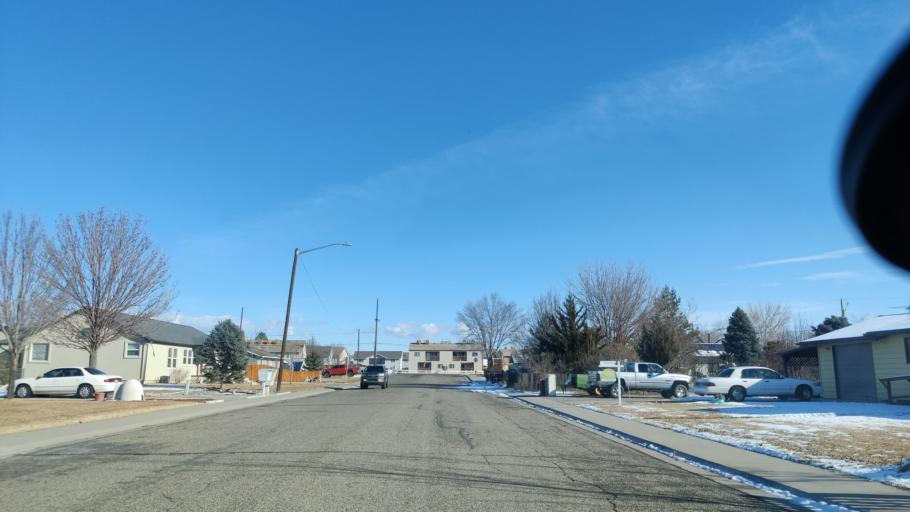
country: US
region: Colorado
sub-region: Mesa County
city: Fruita
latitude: 39.1564
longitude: -108.7214
